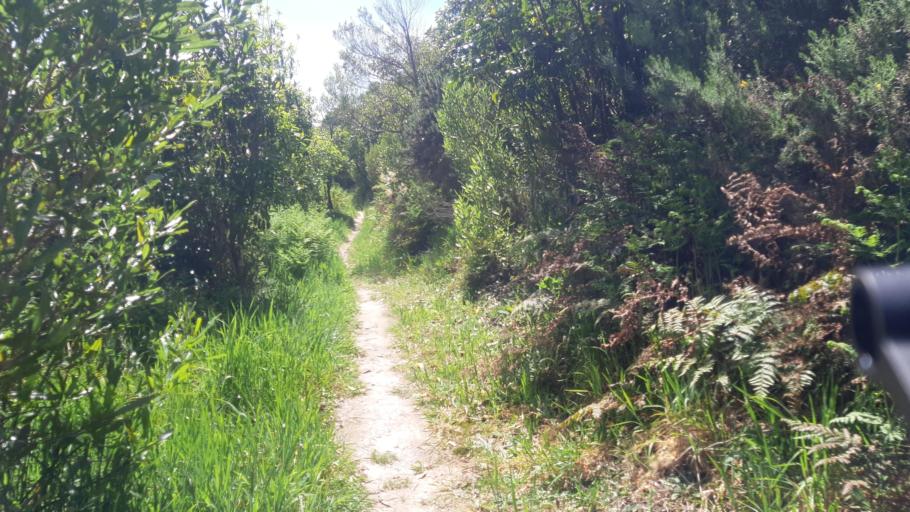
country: NZ
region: Marlborough
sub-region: Marlborough District
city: Picton
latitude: -41.2653
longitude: 174.0300
